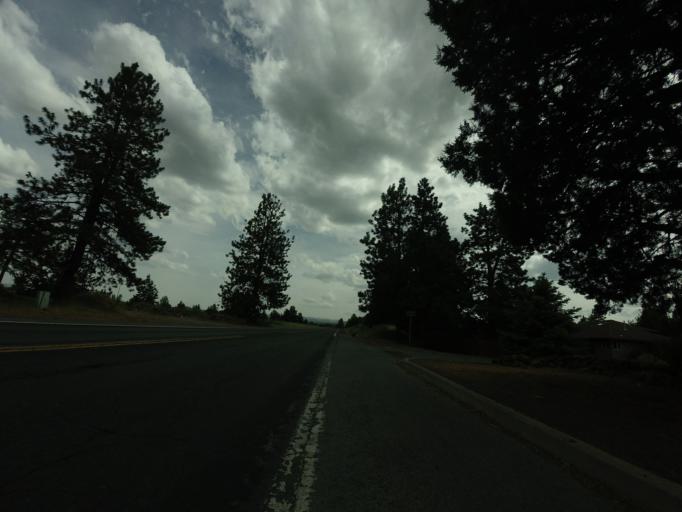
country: US
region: Oregon
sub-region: Deschutes County
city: Bend
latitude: 44.0258
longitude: -121.2639
